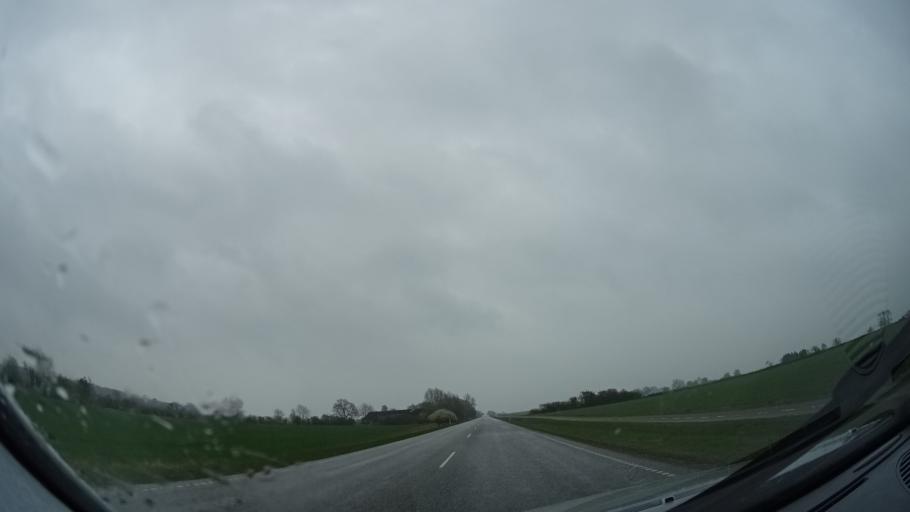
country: DK
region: Zealand
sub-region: Holbaek Kommune
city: Holbaek
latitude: 55.7377
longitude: 11.6271
